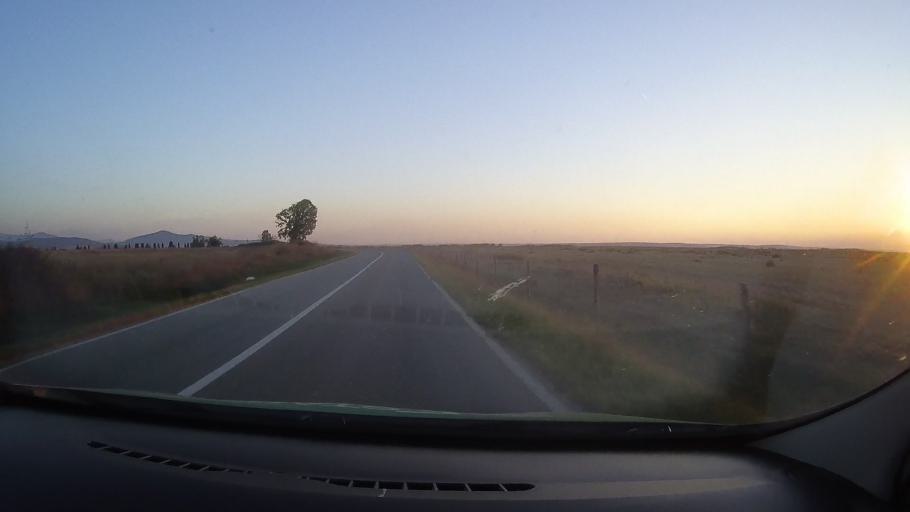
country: RO
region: Timis
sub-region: Comuna Manastiur
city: Manastiur
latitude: 45.8212
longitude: 22.0706
